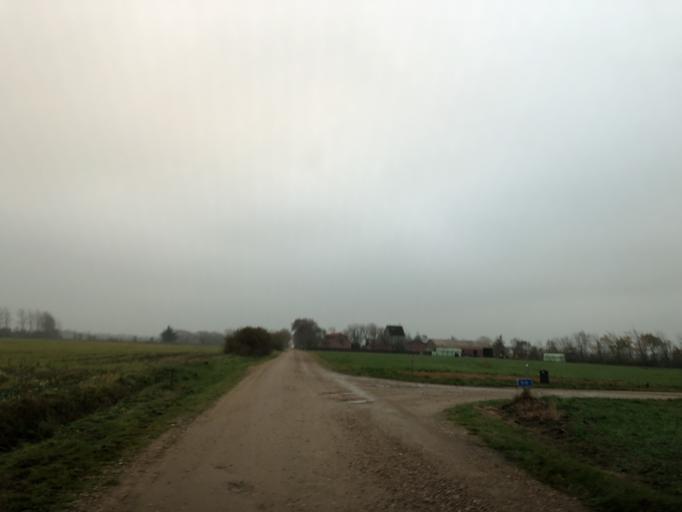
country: DK
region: Central Jutland
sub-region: Herning Kommune
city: Vildbjerg
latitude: 56.2191
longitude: 8.7304
